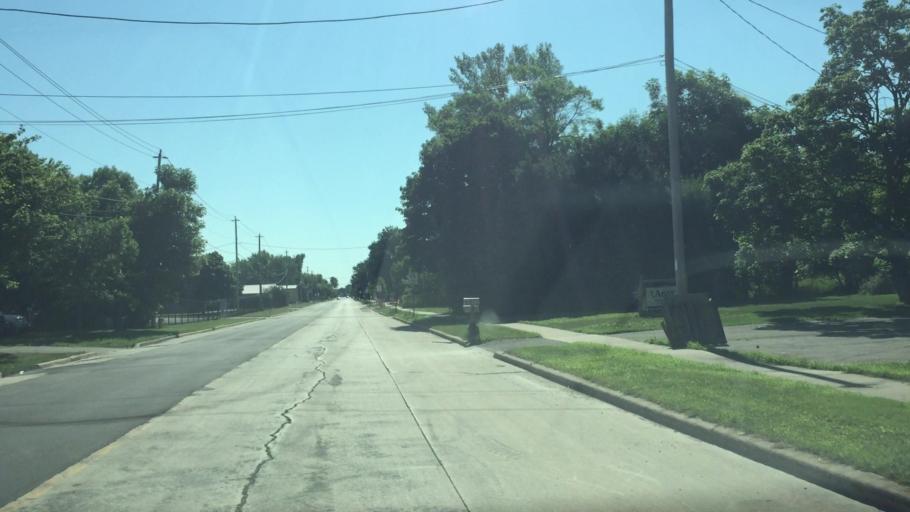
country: US
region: Wisconsin
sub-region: Winnebago County
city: Menasha
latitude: 44.2226
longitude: -88.4431
